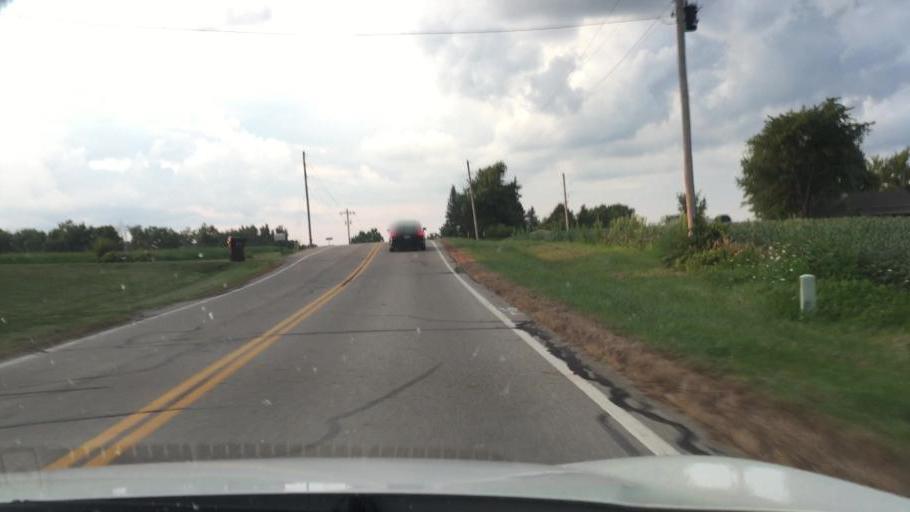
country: US
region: Ohio
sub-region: Champaign County
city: Mechanicsburg
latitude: 40.0473
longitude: -83.5679
